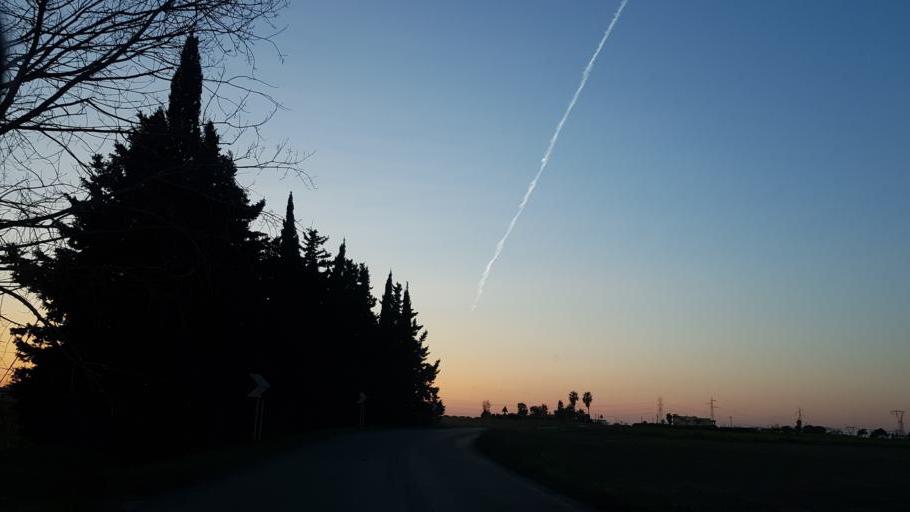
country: IT
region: Apulia
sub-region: Provincia di Brindisi
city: La Rosa
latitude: 40.5919
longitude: 17.9163
